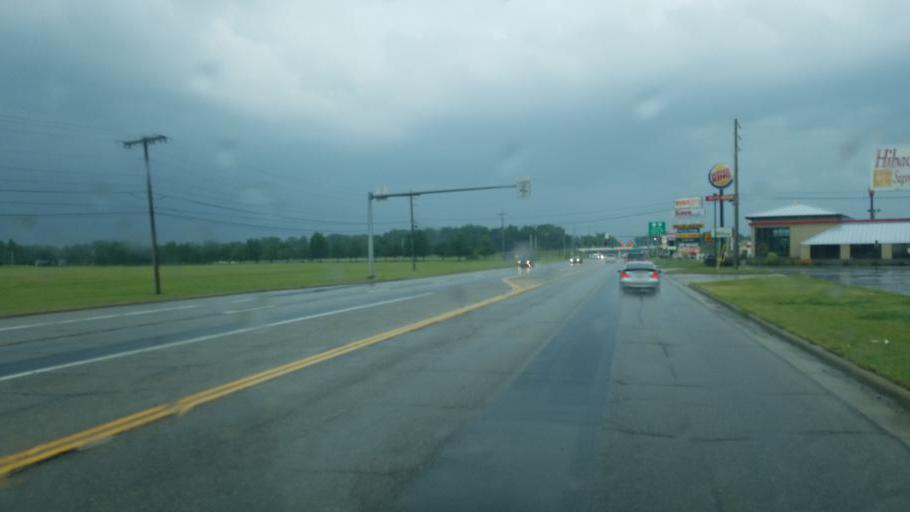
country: US
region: Ohio
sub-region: Trumbull County
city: Champion Heights
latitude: 41.2798
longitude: -80.8436
